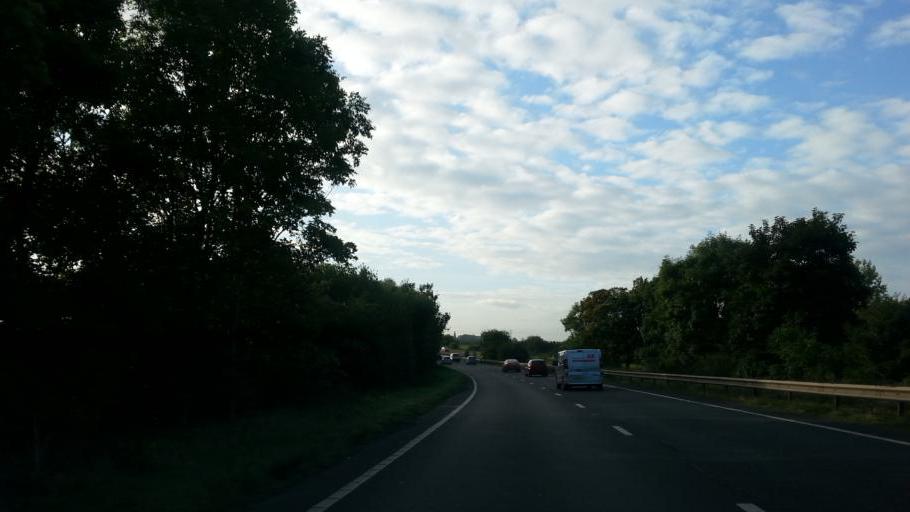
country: GB
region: England
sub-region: Peterborough
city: Wansford
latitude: 52.5798
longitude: -0.4117
